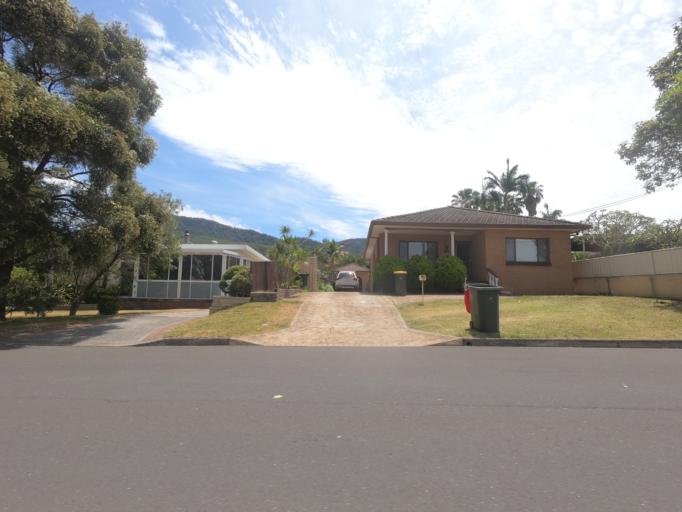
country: AU
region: New South Wales
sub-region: Wollongong
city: Mount Ousley
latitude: -34.3942
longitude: 150.8809
